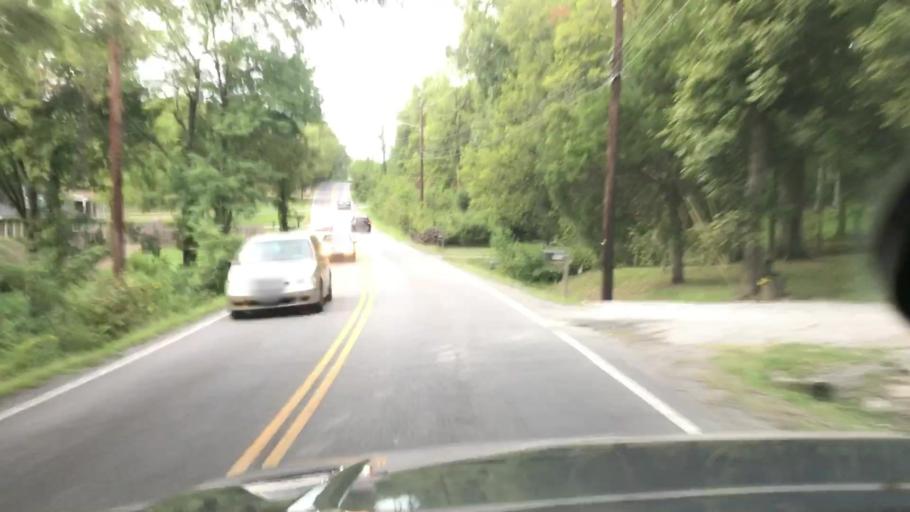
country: US
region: Tennessee
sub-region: Rutherford County
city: La Vergne
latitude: 36.0469
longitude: -86.6267
